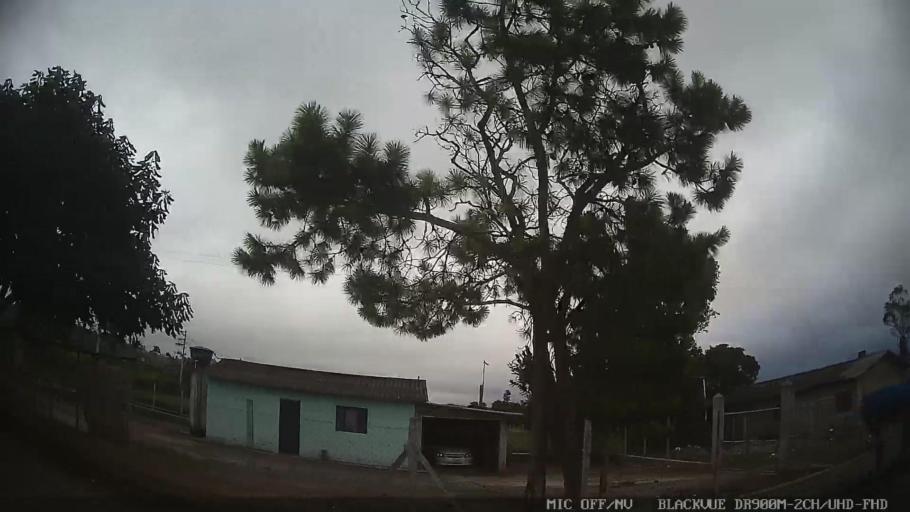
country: BR
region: Sao Paulo
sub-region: Biritiba-Mirim
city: Biritiba Mirim
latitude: -23.5655
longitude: -46.0856
